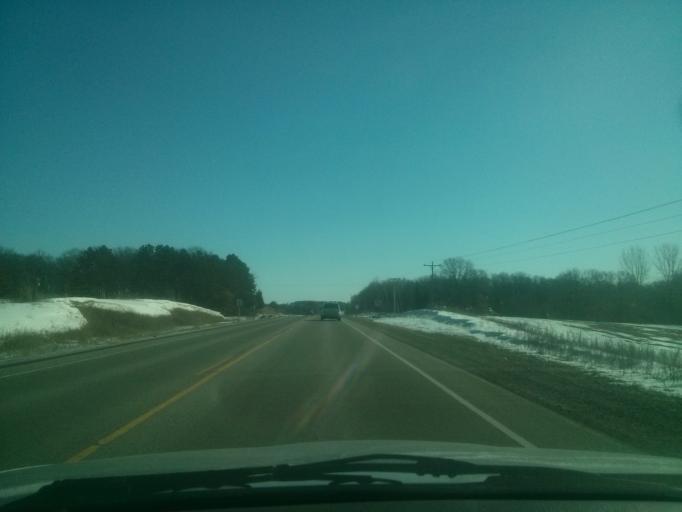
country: US
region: Wisconsin
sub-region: Saint Croix County
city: New Richmond
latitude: 45.1370
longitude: -92.4281
